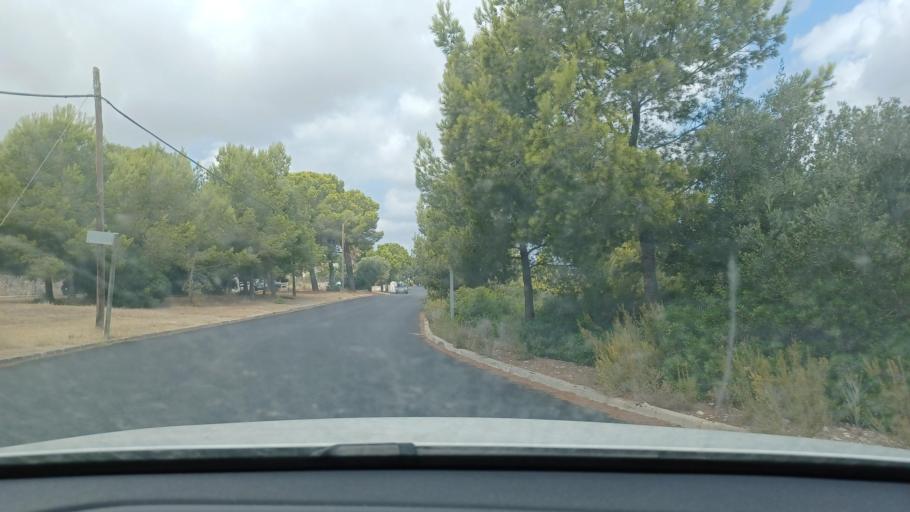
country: ES
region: Catalonia
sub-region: Provincia de Tarragona
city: l'Ametlla de Mar
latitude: 40.9057
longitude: 0.8160
